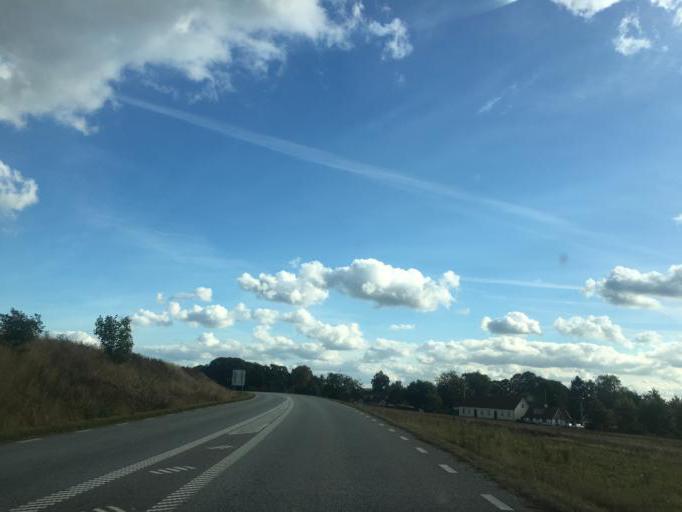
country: SE
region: Skane
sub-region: Eslovs Kommun
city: Eslov
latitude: 55.7642
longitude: 13.3240
